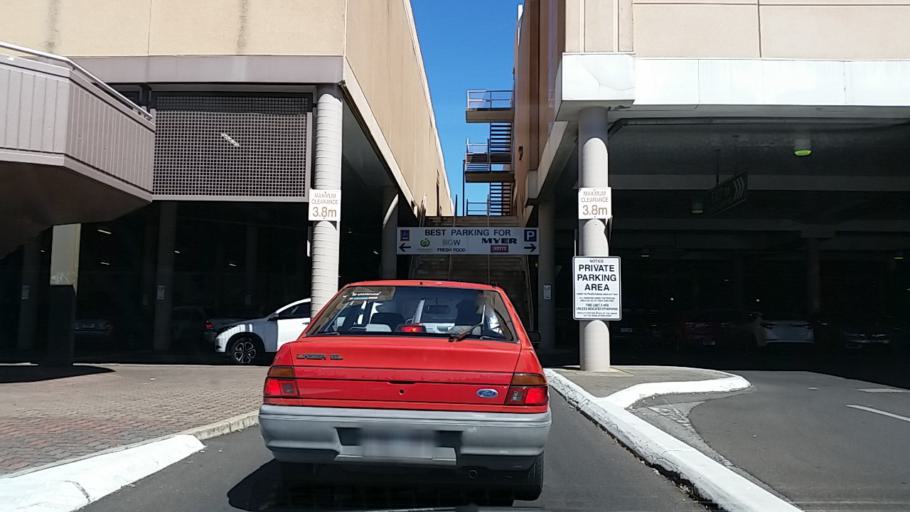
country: AU
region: South Australia
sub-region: Tea Tree Gully
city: Modbury
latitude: -34.8307
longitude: 138.6902
